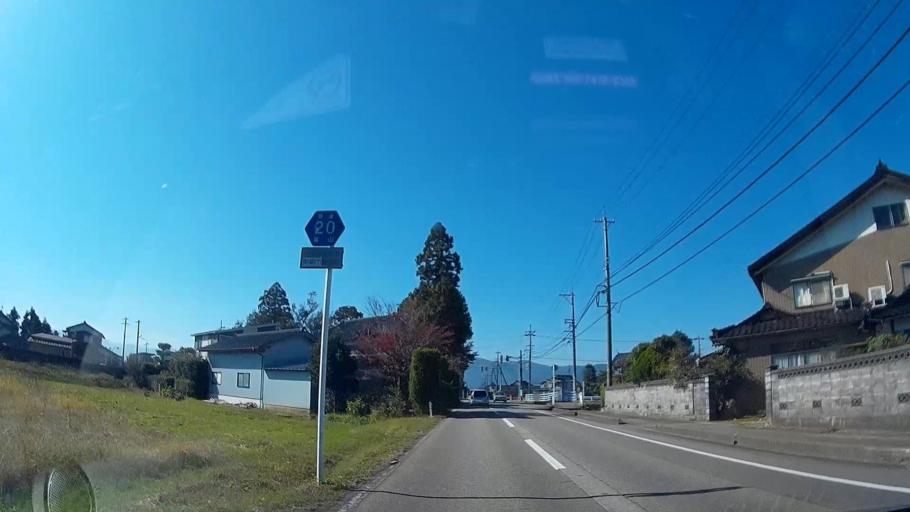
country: JP
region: Toyama
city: Nanto-shi
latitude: 36.5767
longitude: 136.8985
